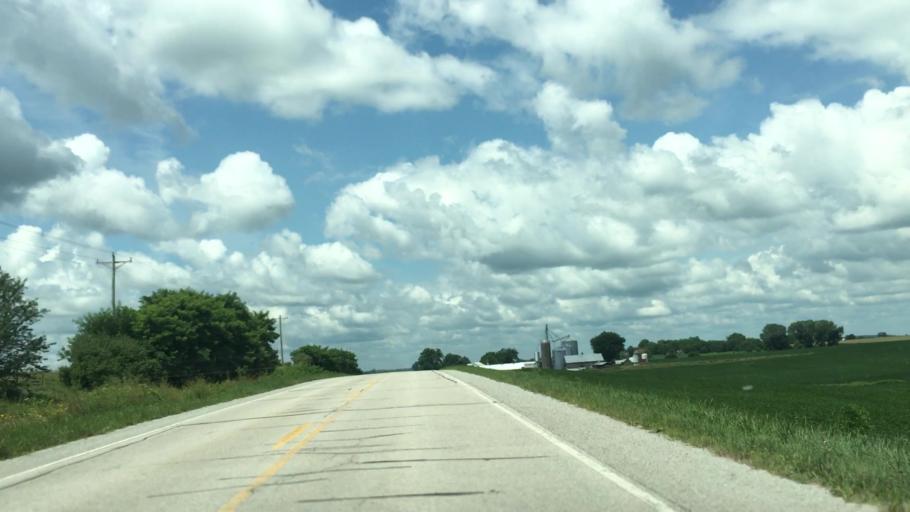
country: US
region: Iowa
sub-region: Johnson County
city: Solon
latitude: 41.8308
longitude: -91.4854
